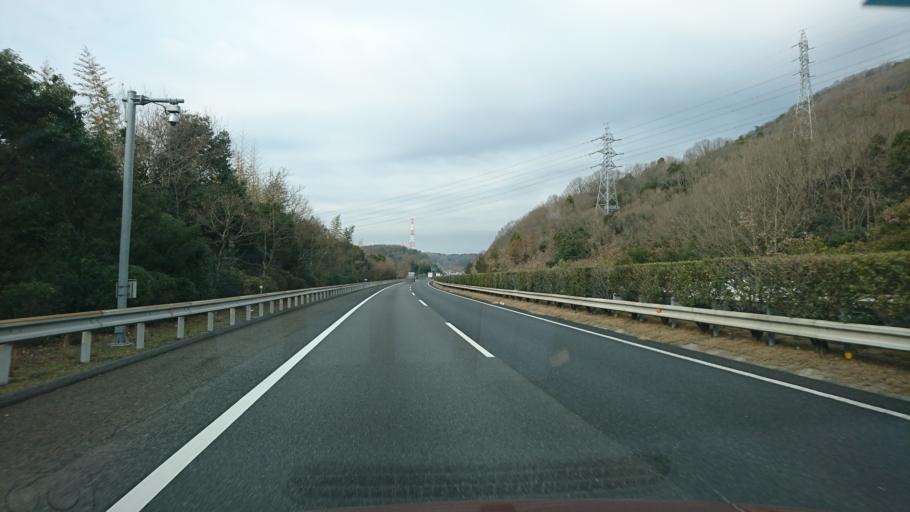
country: JP
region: Okayama
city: Kasaoka
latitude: 34.5322
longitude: 133.5298
